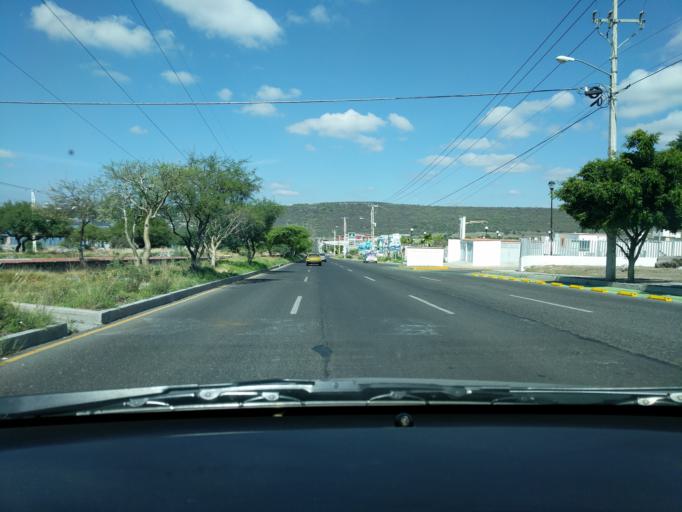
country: MX
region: Queretaro
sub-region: Queretaro
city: Patria Nueva
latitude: 20.6434
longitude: -100.4892
